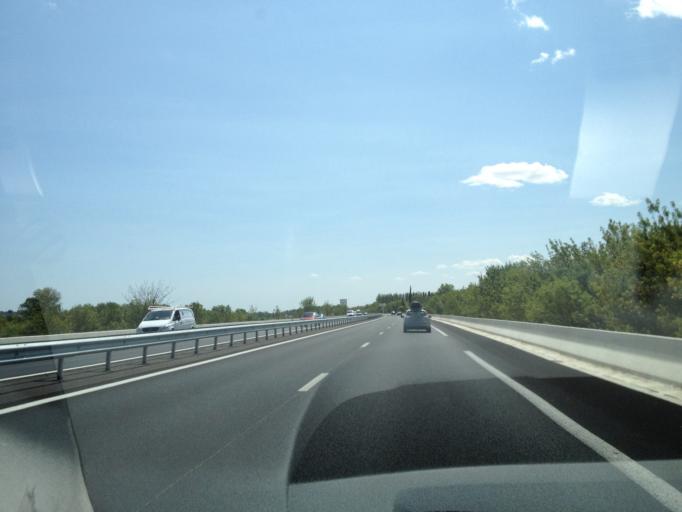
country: FR
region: Languedoc-Roussillon
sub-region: Departement de l'Herault
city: Pezenas
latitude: 43.4682
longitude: 3.4335
